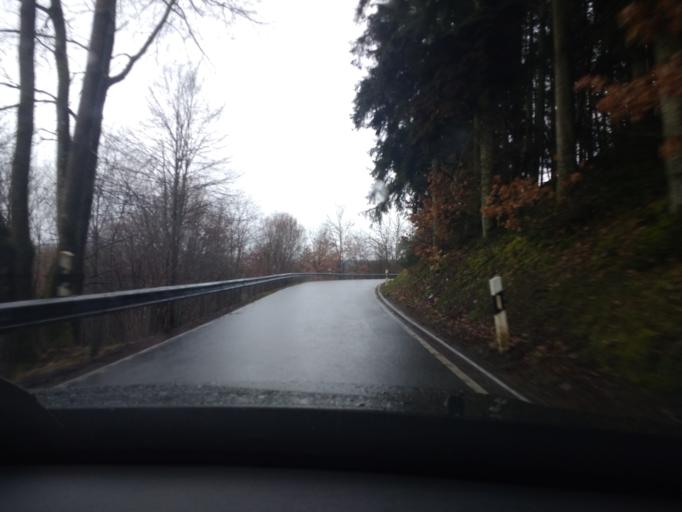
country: DE
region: Rheinland-Pfalz
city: Hinzenburg
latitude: 49.6788
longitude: 6.7266
